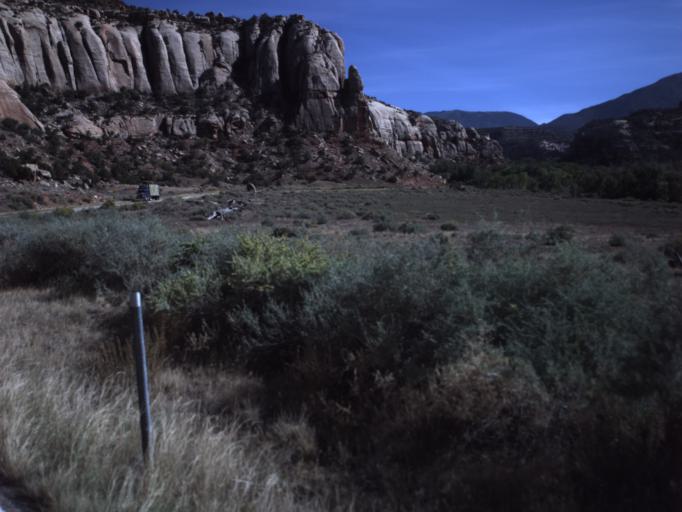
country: US
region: Utah
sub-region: San Juan County
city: Monticello
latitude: 38.0332
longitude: -109.5428
